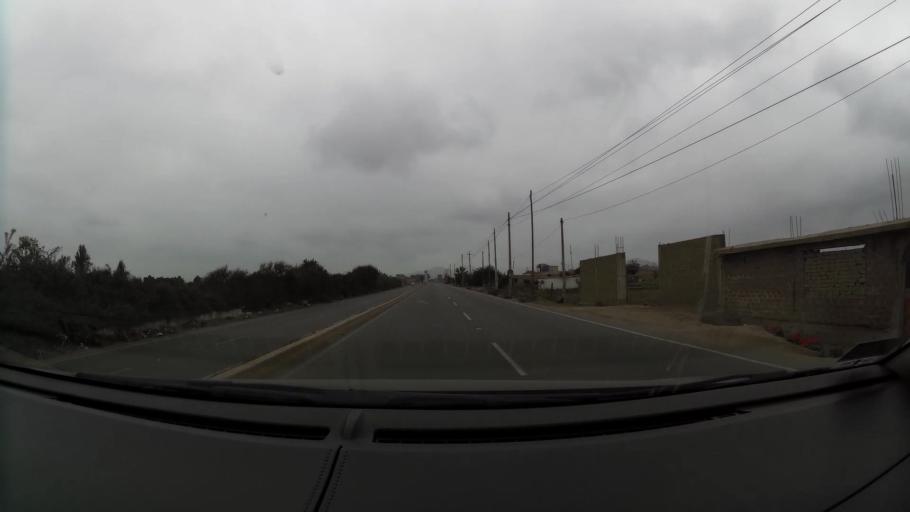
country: PE
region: Lima
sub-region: Provincia de Huaral
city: Huaral
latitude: -11.5096
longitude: -77.2322
